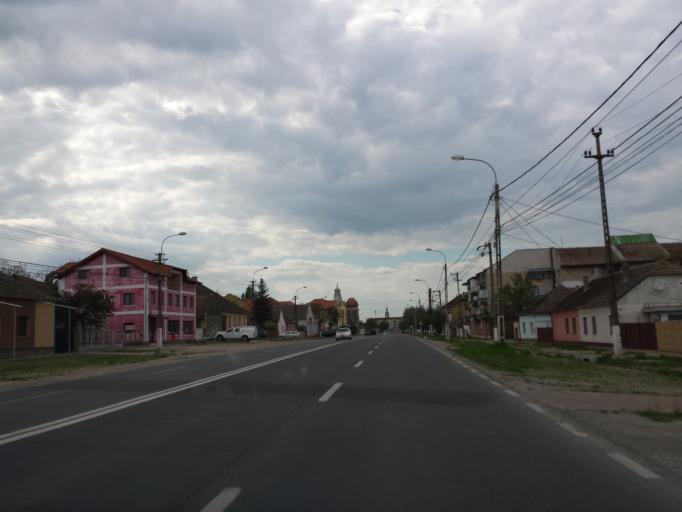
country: RO
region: Timis
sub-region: Oras Sannicolau Mare
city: Sannicolau Mare
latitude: 46.0675
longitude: 20.6392
